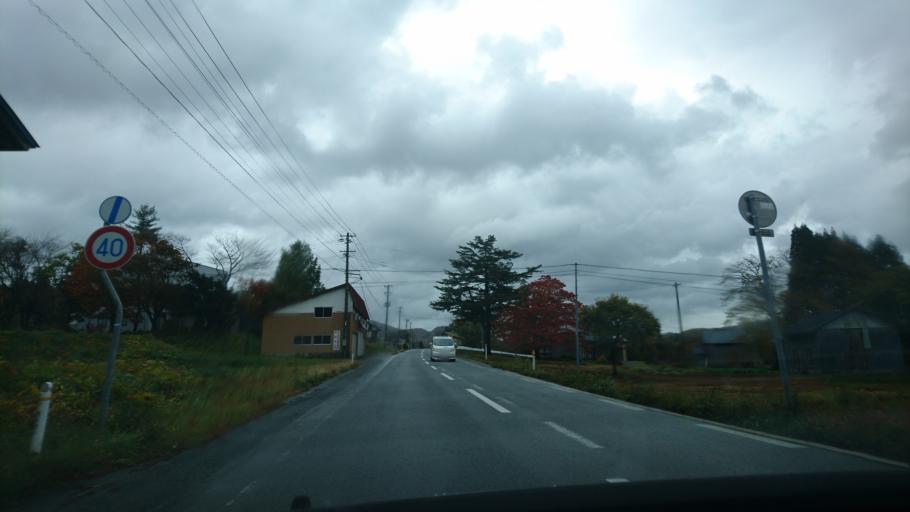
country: JP
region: Akita
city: Kakunodatemachi
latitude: 39.4607
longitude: 140.7751
